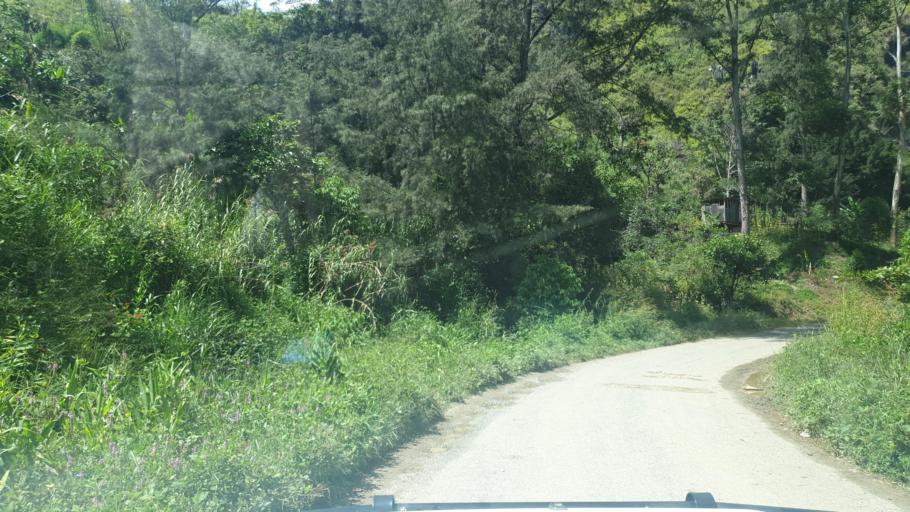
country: PG
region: Chimbu
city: Kundiawa
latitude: -6.1470
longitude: 145.1344
